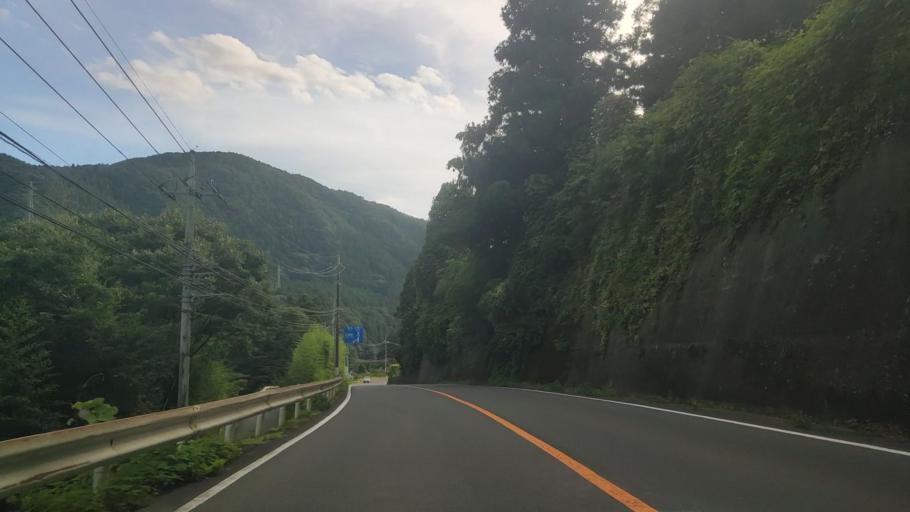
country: JP
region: Gunma
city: Omamacho-omama
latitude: 36.5029
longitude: 139.2922
